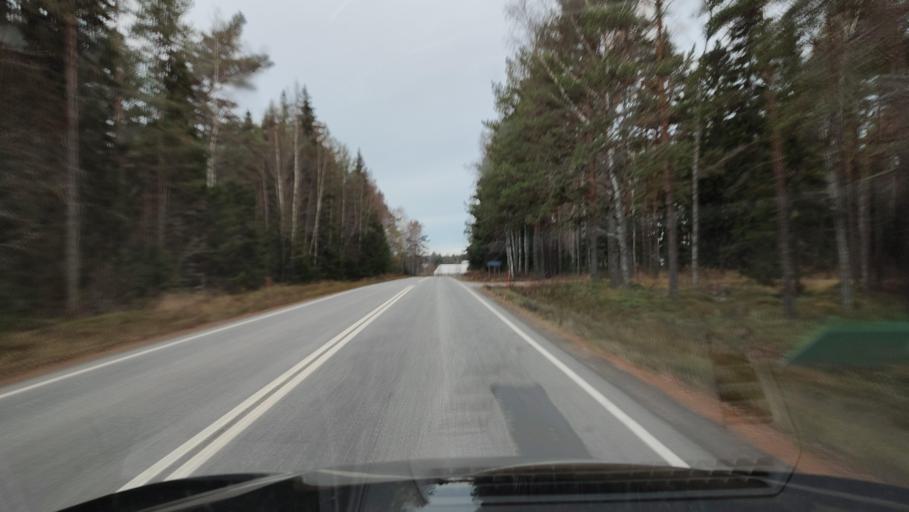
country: FI
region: Ostrobothnia
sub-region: Sydosterbotten
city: Naerpes
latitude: 62.4018
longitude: 21.3585
